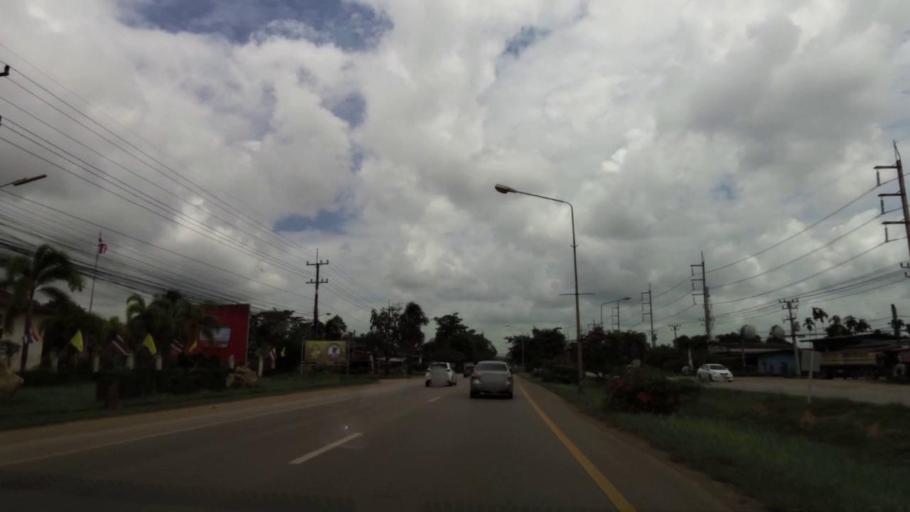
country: TH
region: Chanthaburi
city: Na Yai Am
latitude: 12.7837
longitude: 101.7966
